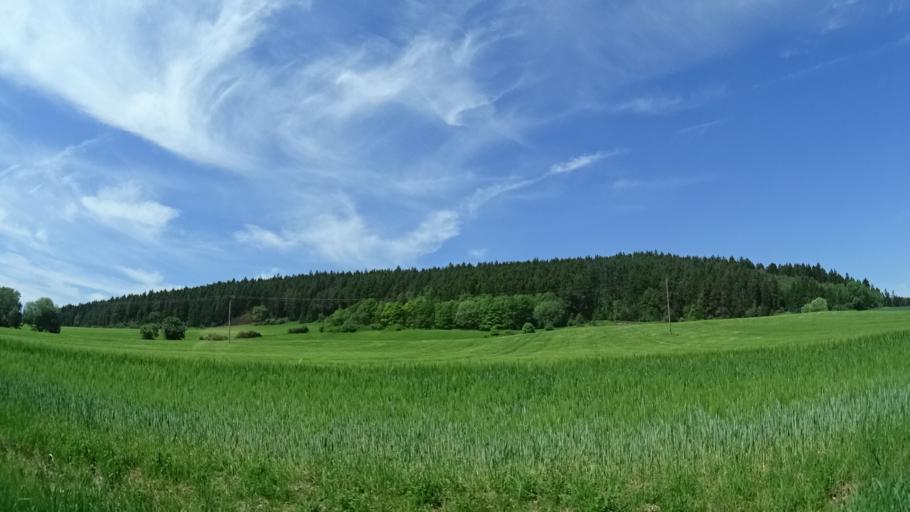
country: DE
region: Thuringia
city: Plaue
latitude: 50.7460
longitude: 10.9415
